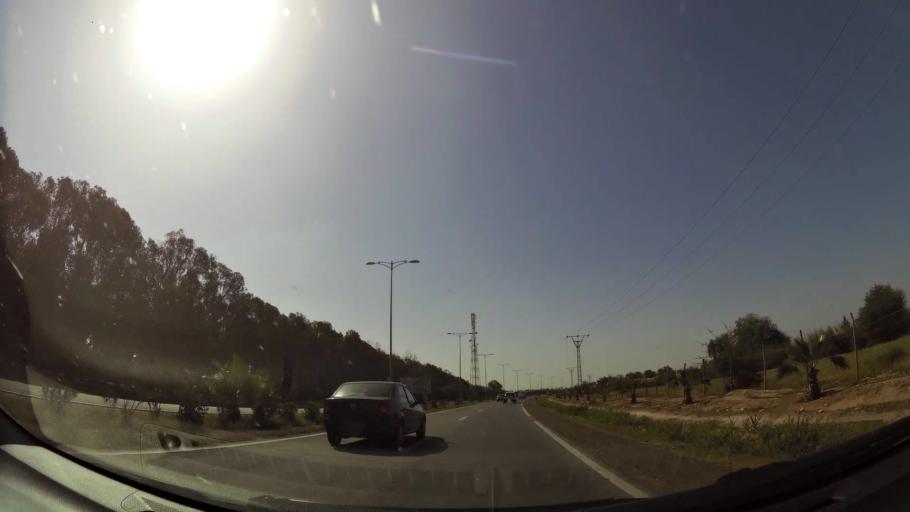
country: MA
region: Souss-Massa-Draa
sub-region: Inezgane-Ait Mellou
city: Inezgane
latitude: 30.3493
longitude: -9.4797
